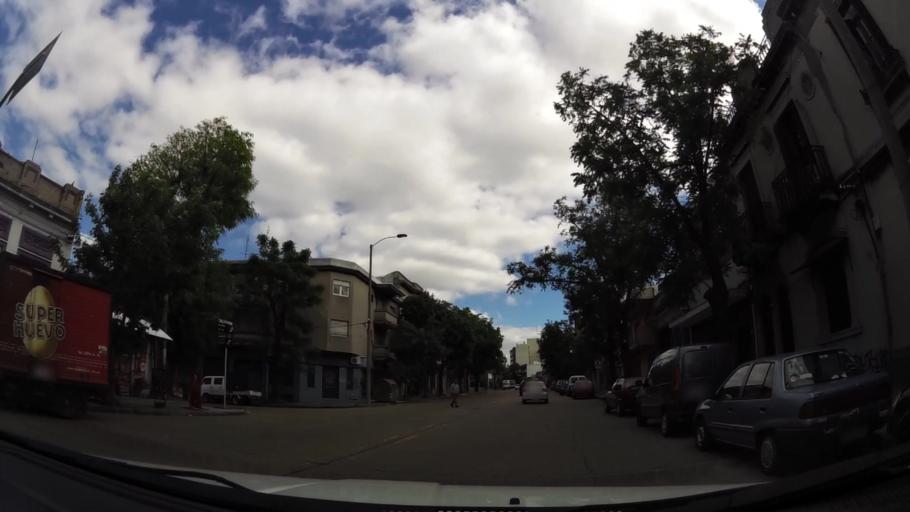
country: UY
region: Montevideo
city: Montevideo
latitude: -34.8777
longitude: -56.1872
